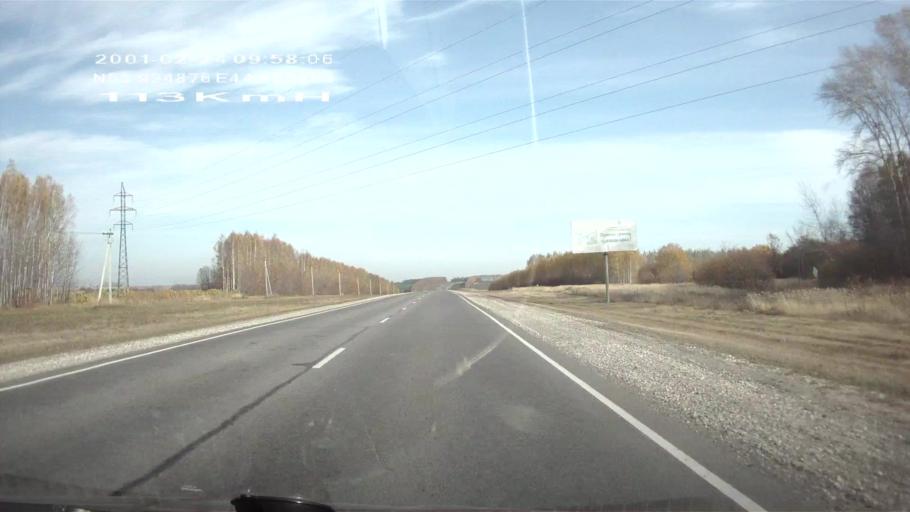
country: RU
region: Penza
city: Issa
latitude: 53.9254
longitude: 44.8662
